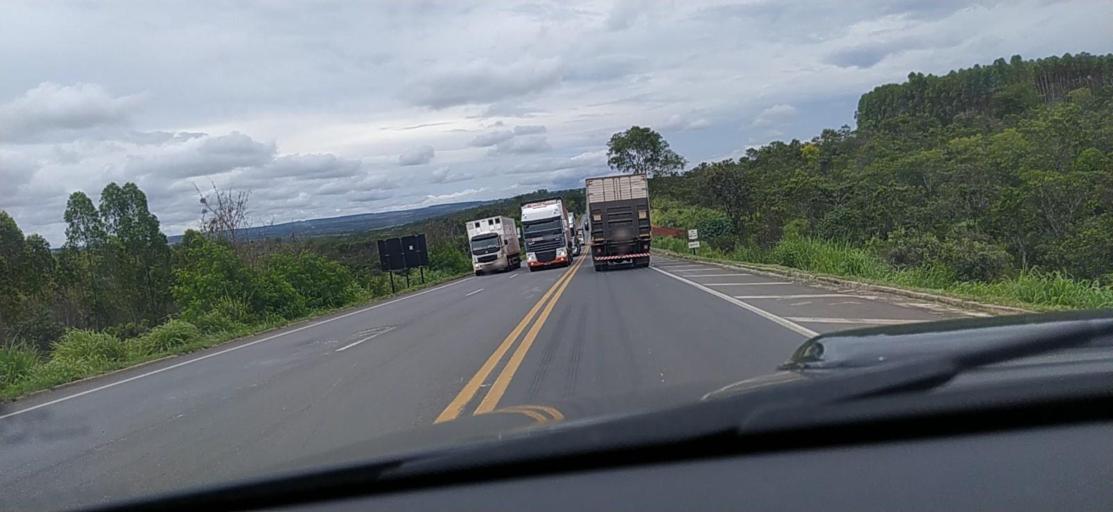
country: BR
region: Minas Gerais
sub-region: Curvelo
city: Curvelo
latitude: -18.7029
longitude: -44.4402
